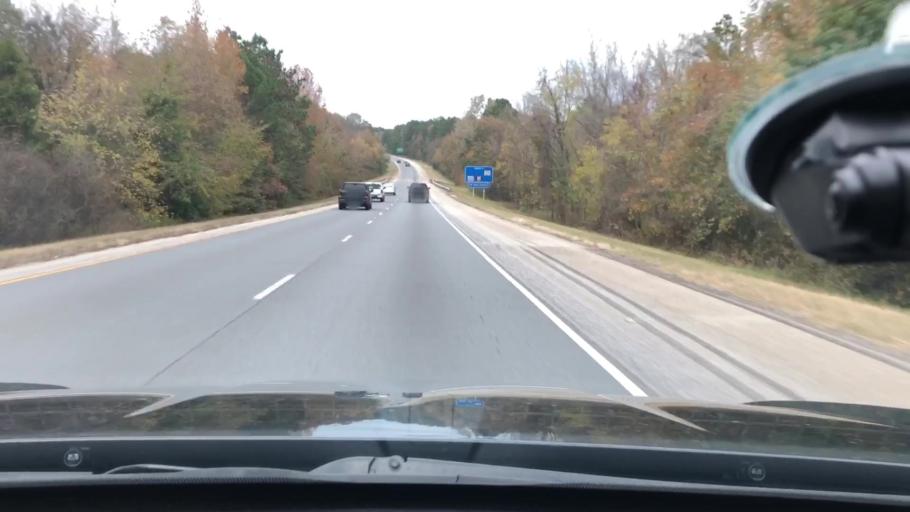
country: US
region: Arkansas
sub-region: Clark County
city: Arkadelphia
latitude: 34.0964
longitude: -93.1053
